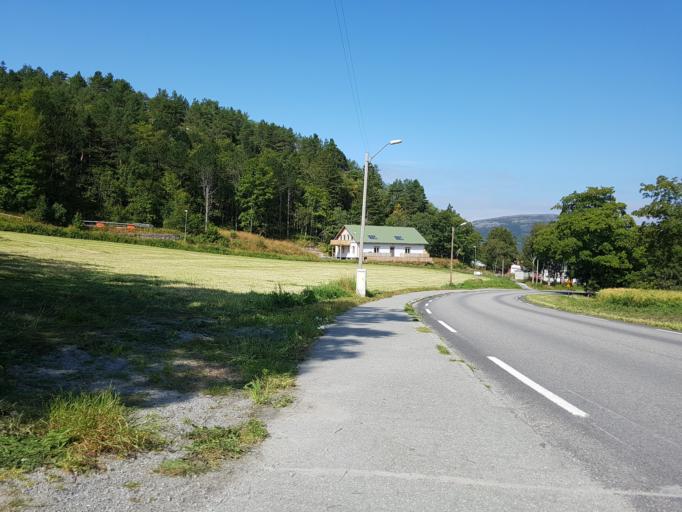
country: NO
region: Sor-Trondelag
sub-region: Agdenes
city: Lensvik
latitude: 63.6295
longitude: 9.8247
